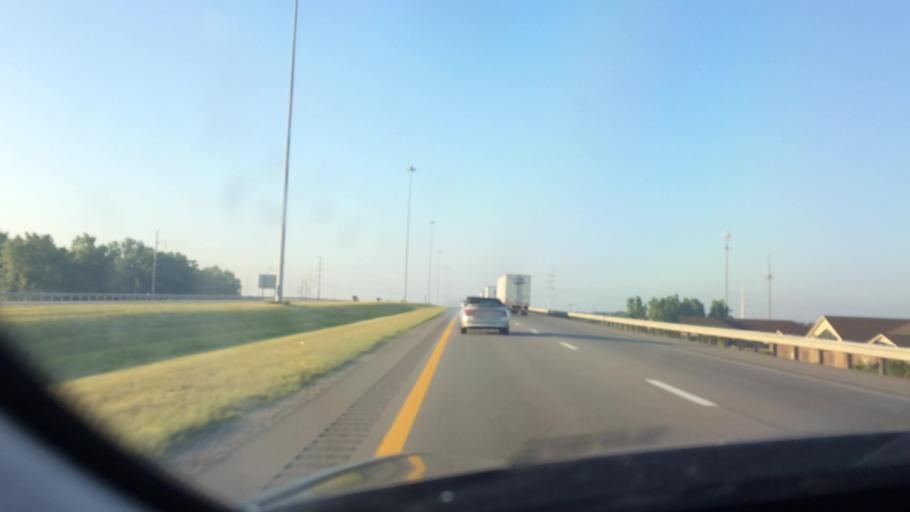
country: US
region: Ohio
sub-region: Lucas County
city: Maumee
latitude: 41.5629
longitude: -83.6896
